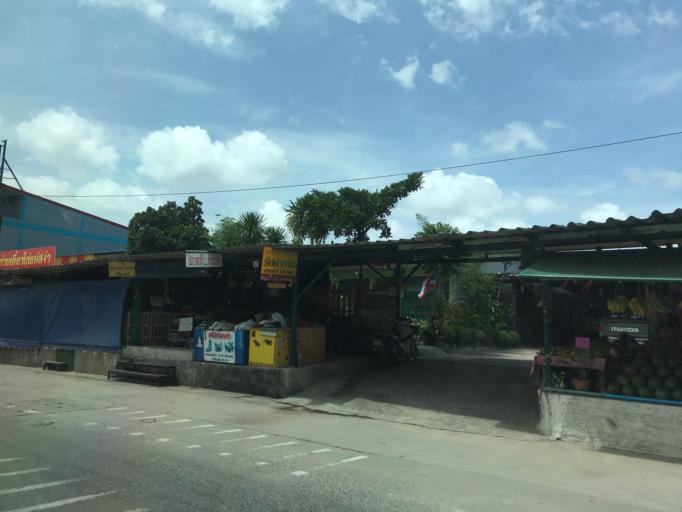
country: TH
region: Chon Buri
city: Si Racha
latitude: 13.1472
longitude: 100.9510
